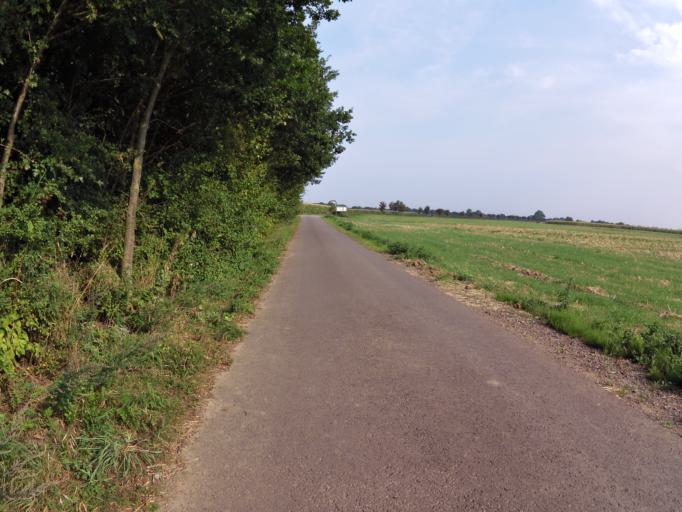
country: DE
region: Lower Saxony
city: Raddestorf
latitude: 52.4652
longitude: 9.0172
